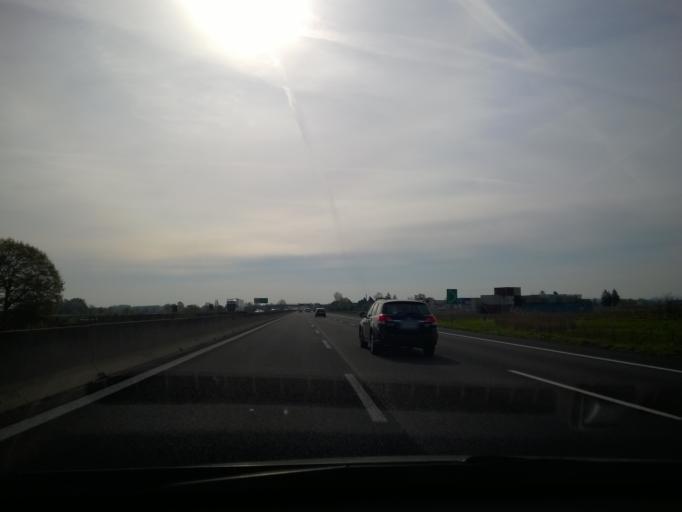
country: IT
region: Emilia-Romagna
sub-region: Forli-Cesena
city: Santa Maria Nuova
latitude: 44.2038
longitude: 12.2032
